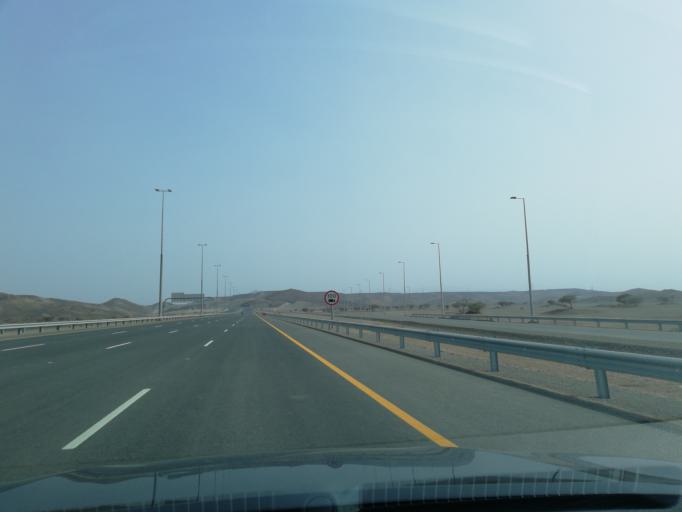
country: OM
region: Al Batinah
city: Al Liwa'
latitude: 24.3652
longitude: 56.5524
